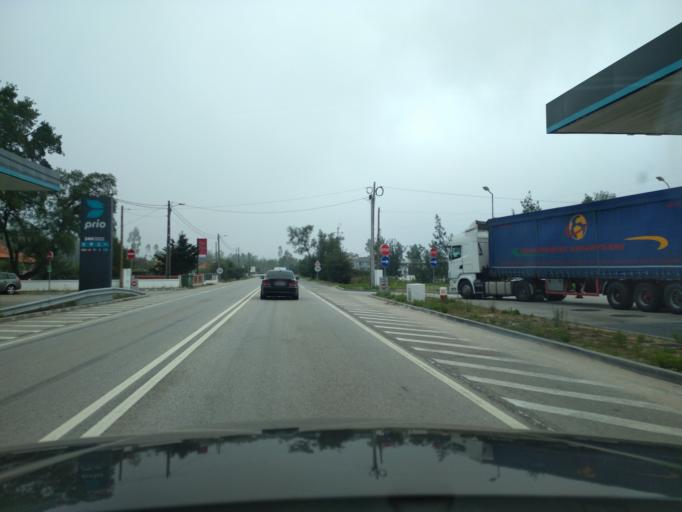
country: PT
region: Aveiro
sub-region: Mealhada
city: Pampilhosa do Botao
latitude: 40.3335
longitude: -8.4506
